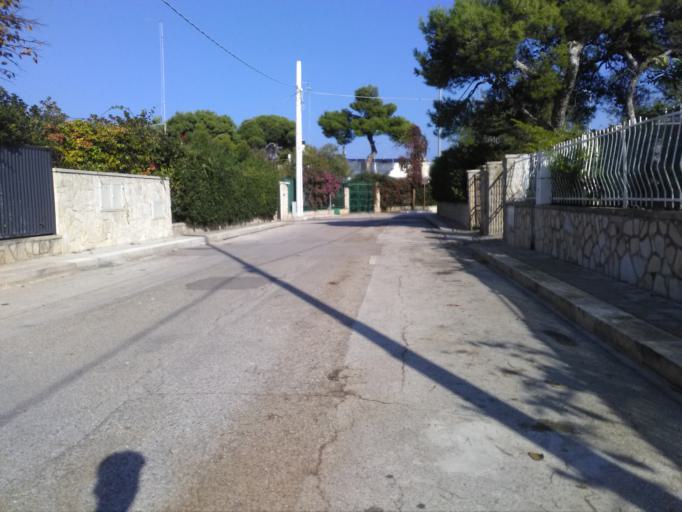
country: IT
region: Apulia
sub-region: Provincia di Bari
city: San Paolo
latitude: 41.1588
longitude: 16.7684
